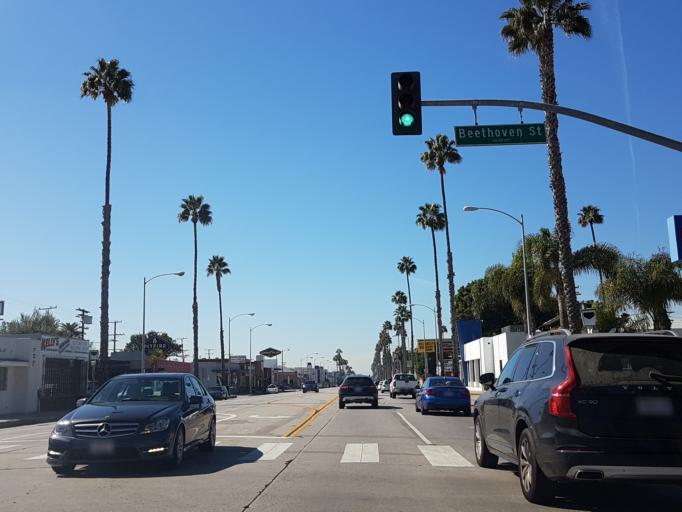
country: US
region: California
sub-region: Los Angeles County
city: Marina del Rey
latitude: 33.9953
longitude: -118.4382
